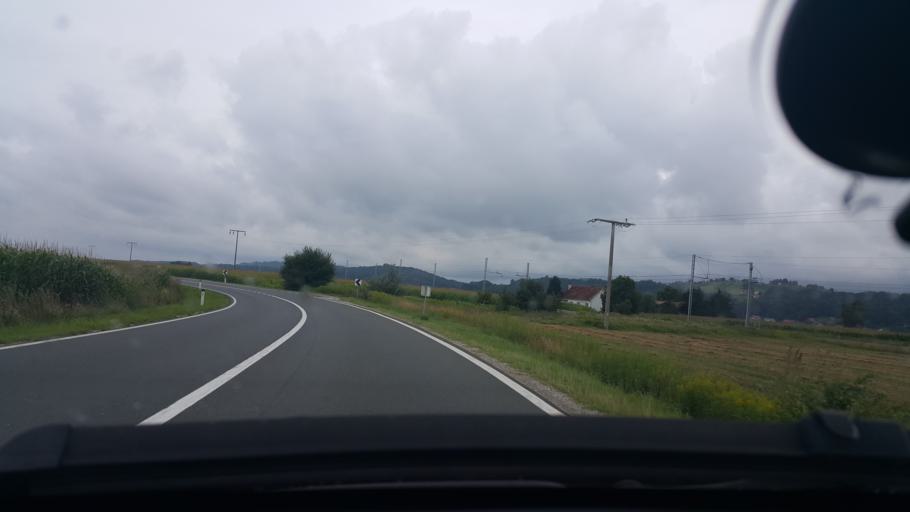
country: SI
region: Zavrc
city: Zavrc
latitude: 46.4168
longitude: 16.0831
